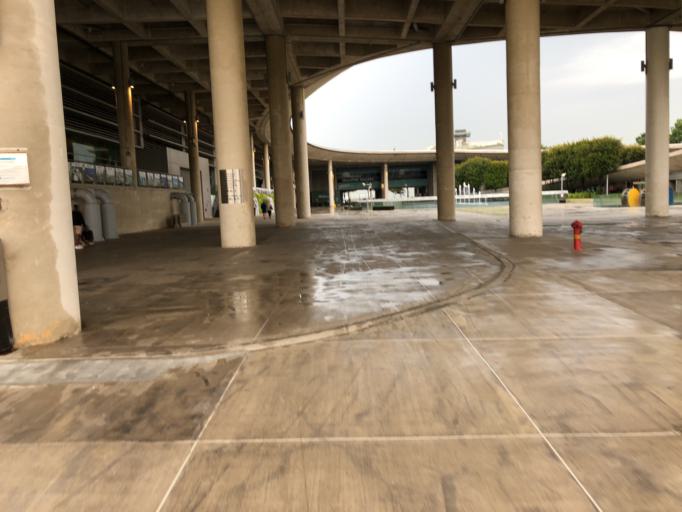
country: SG
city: Singapore
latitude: 1.2814
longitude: 103.8702
